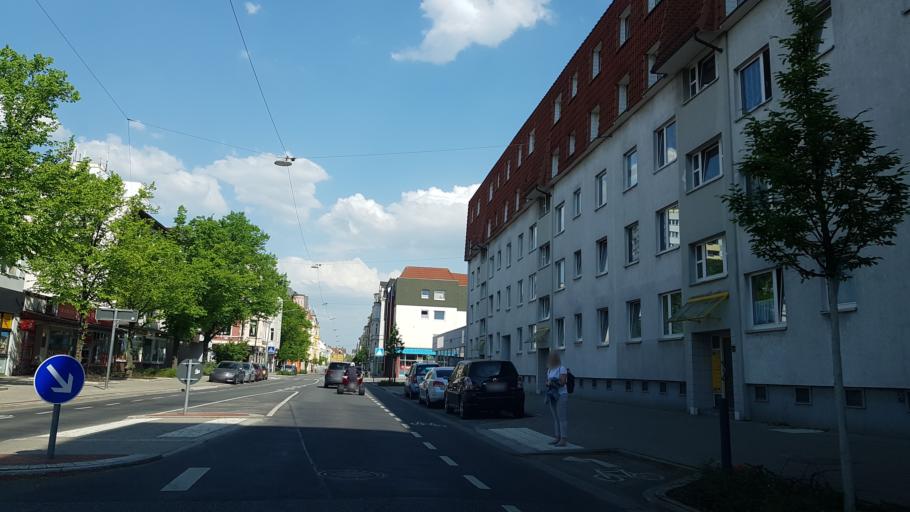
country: DE
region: Bremen
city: Bremerhaven
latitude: 53.5605
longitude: 8.5748
